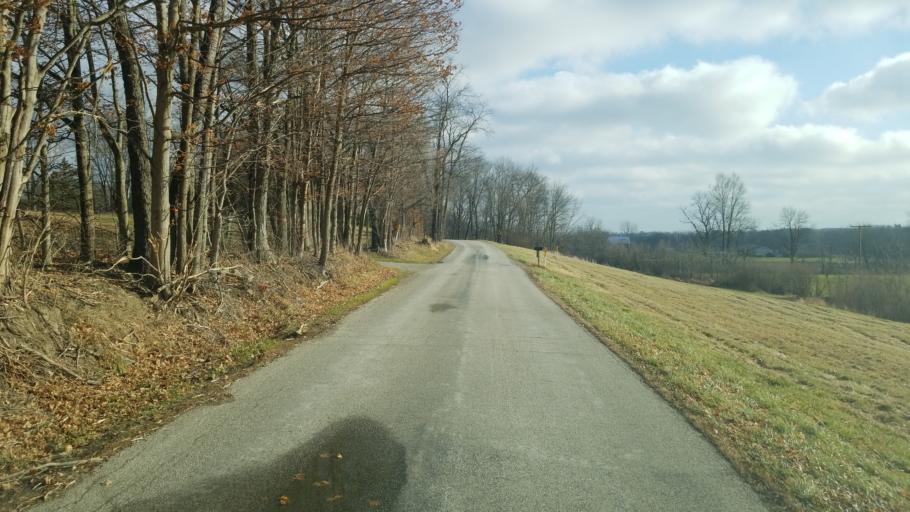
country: US
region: Ohio
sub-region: Richland County
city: Lincoln Heights
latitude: 40.8143
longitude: -82.4411
